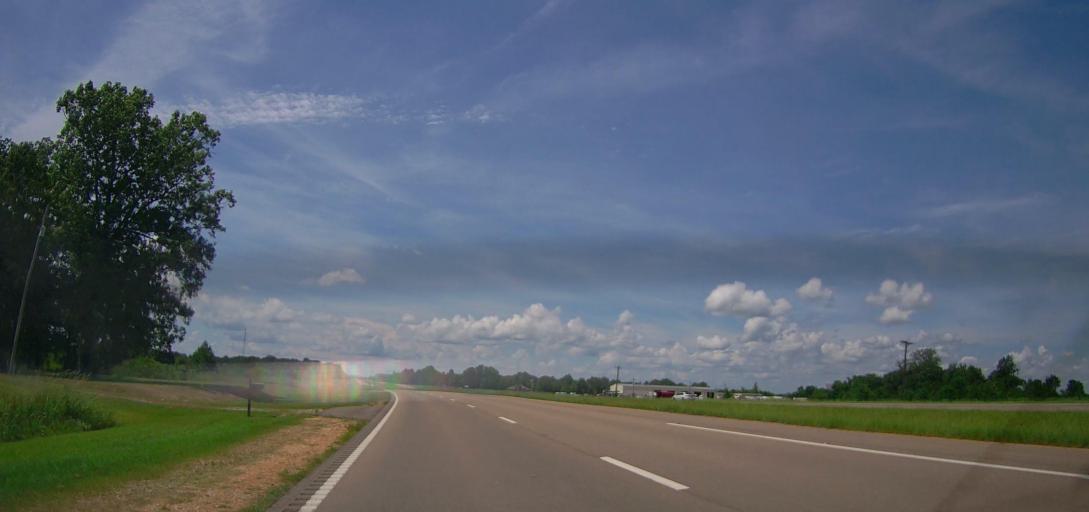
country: US
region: Mississippi
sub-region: Lee County
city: Nettleton
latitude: 33.9774
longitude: -88.6146
